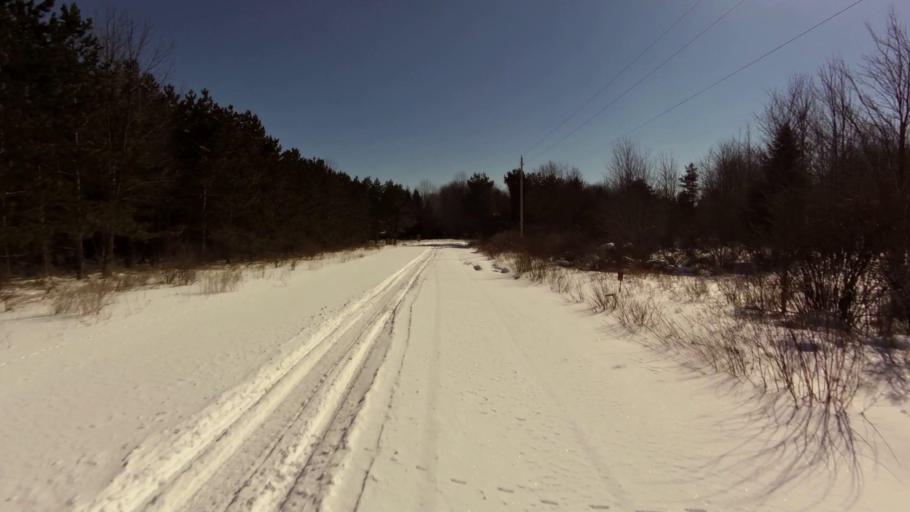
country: US
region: New York
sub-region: Allegany County
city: Cuba
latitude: 42.3313
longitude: -78.2850
